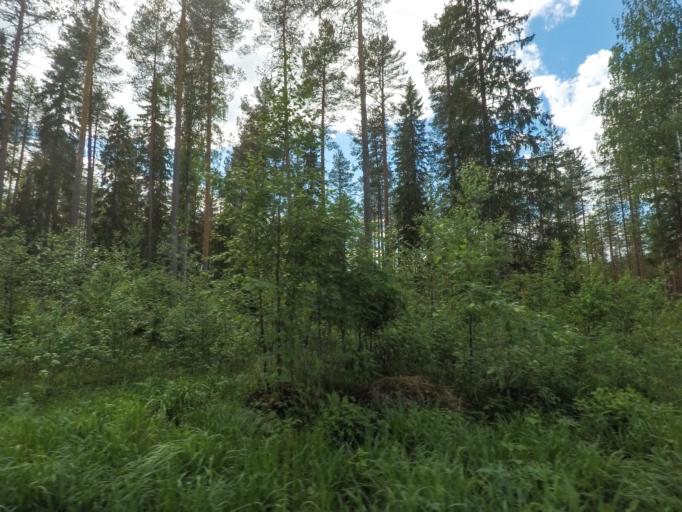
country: FI
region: Central Finland
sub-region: Jyvaeskylae
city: Hankasalmi
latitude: 62.4082
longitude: 26.6512
